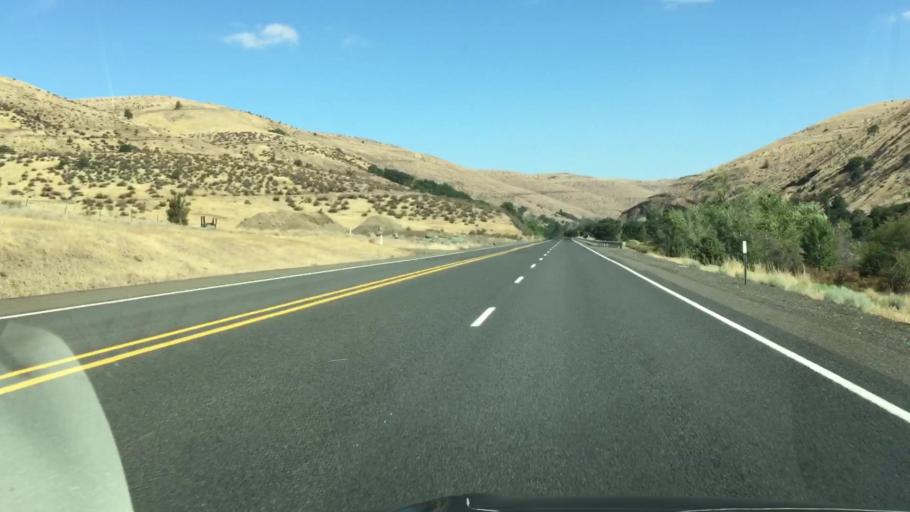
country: US
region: Oregon
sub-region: Wasco County
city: The Dalles
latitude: 45.2635
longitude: -121.1909
